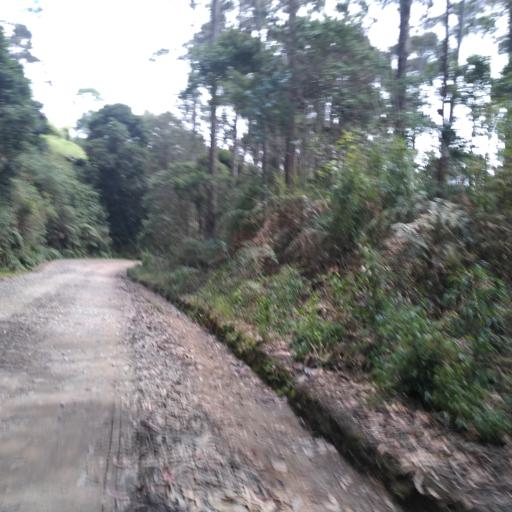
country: CO
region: Boyaca
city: Duitama
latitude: 5.9460
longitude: -73.1423
